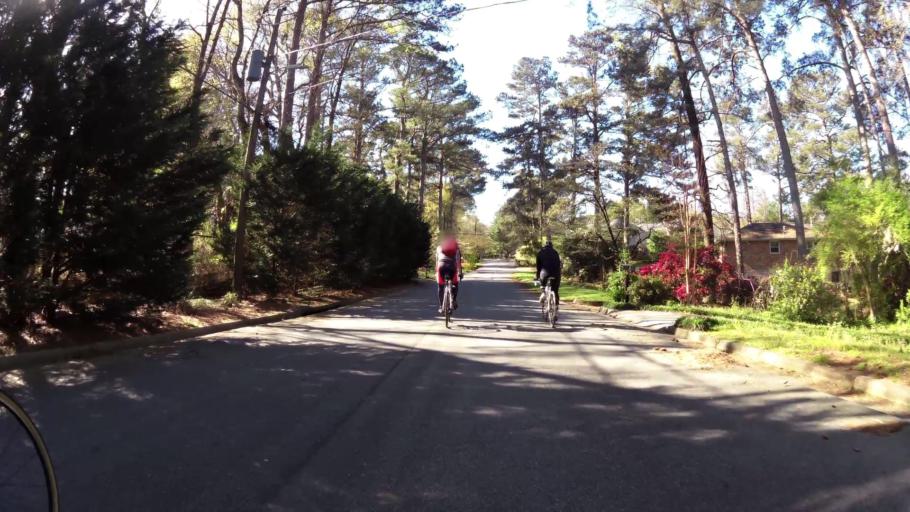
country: US
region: Georgia
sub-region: DeKalb County
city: Clarkston
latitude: 33.8302
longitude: -84.2658
